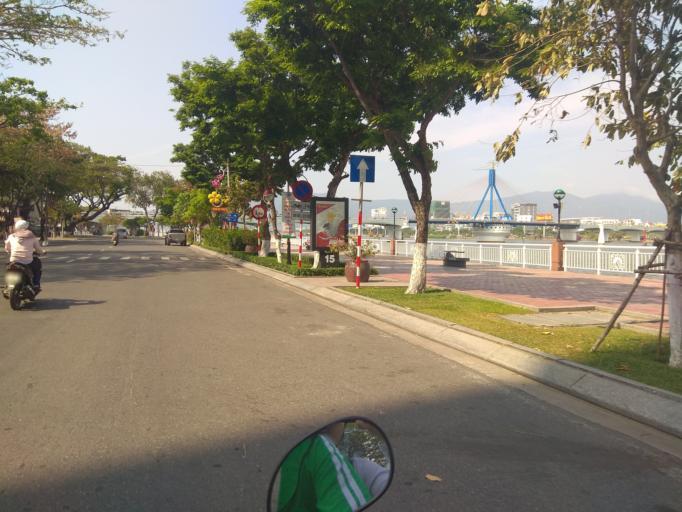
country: VN
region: Da Nang
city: Da Nang
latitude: 16.0701
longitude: 108.2251
